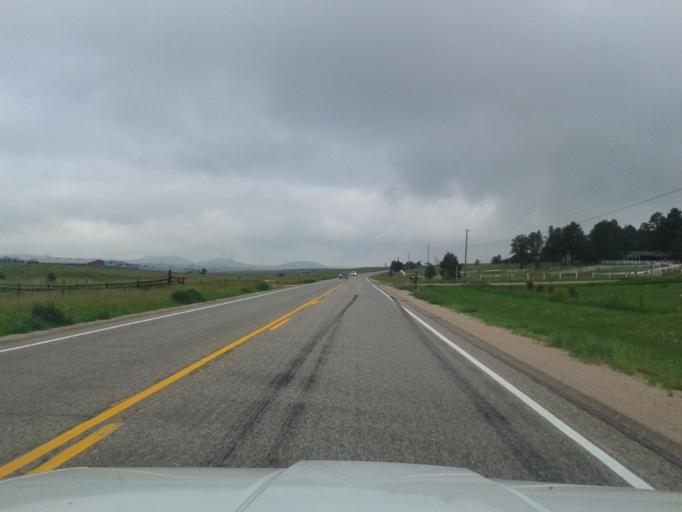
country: US
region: Colorado
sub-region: El Paso County
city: Gleneagle
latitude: 39.0900
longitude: -104.7707
